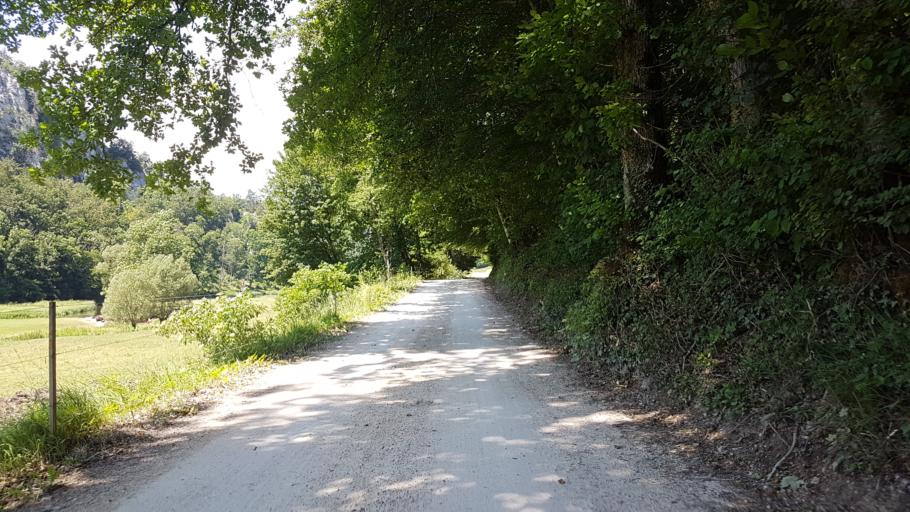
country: DE
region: Baden-Wuerttemberg
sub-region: Tuebingen Region
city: Beuron
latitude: 48.0256
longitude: 8.9653
